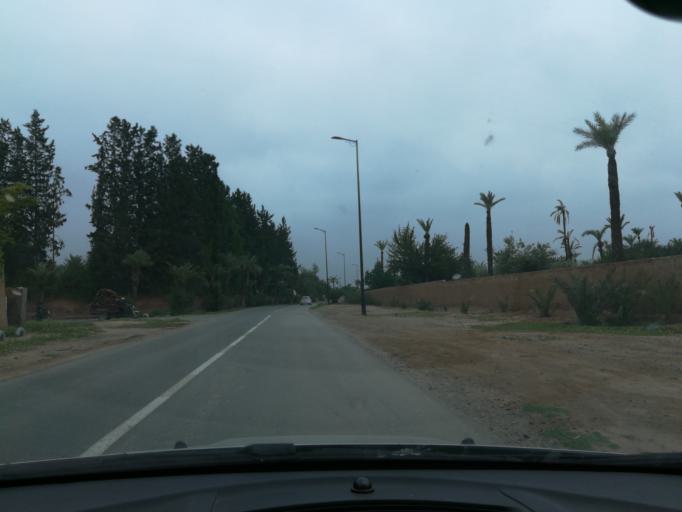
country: MA
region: Marrakech-Tensift-Al Haouz
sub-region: Marrakech
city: Marrakesh
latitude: 31.6521
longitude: -7.9743
